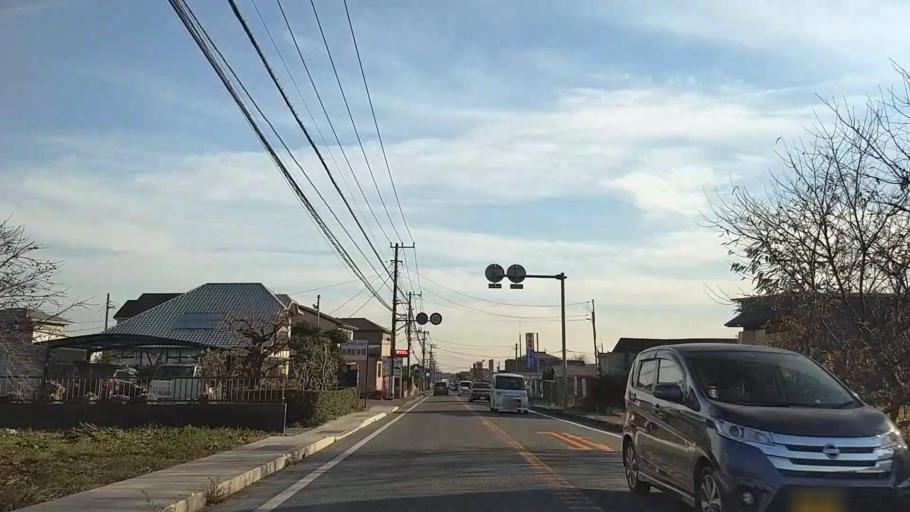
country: JP
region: Kanagawa
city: Zama
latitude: 35.5027
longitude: 139.3111
